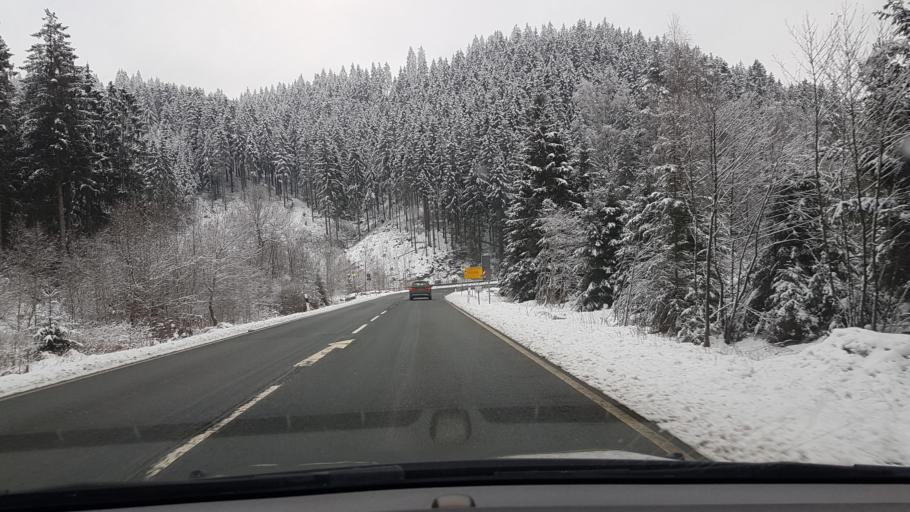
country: DE
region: Lower Saxony
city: Wildemann
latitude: 51.8136
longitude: 10.2797
